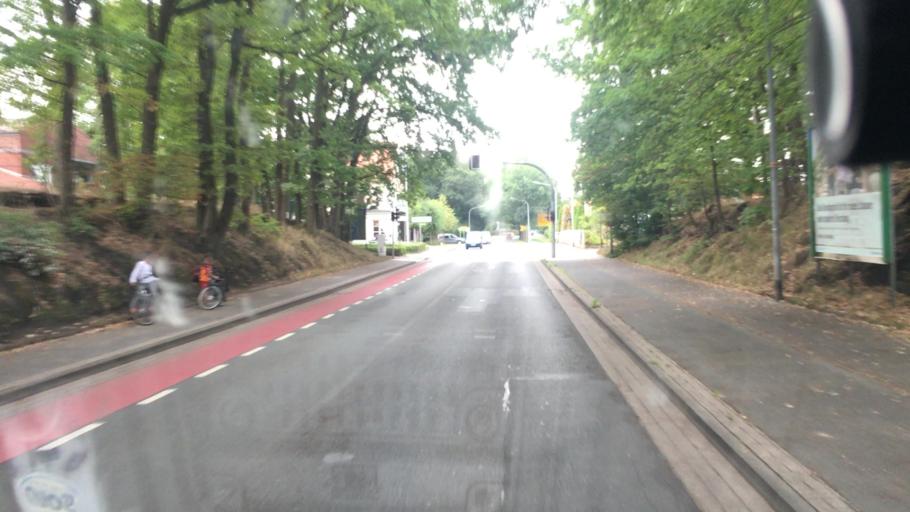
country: DE
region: Lower Saxony
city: Lohne
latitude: 52.6536
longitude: 8.2424
